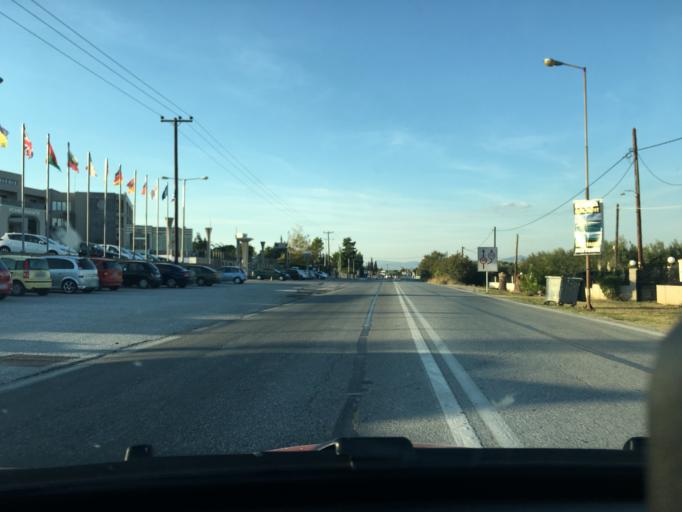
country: GR
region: Central Macedonia
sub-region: Nomos Chalkidikis
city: Nea Potidhaia
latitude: 40.2061
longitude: 23.3234
